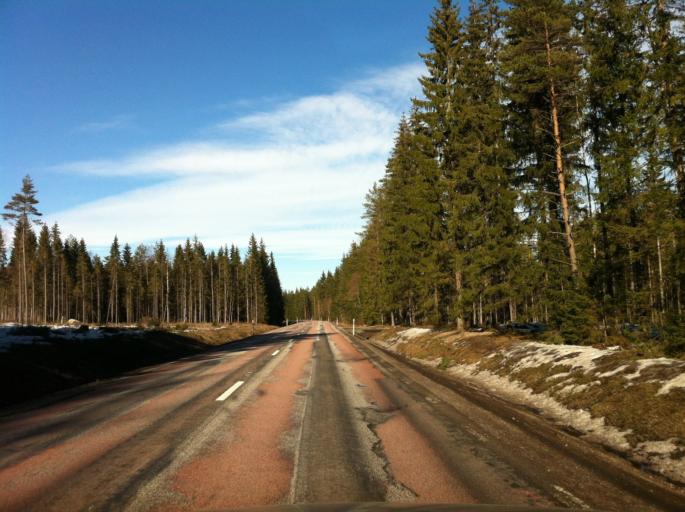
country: SE
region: Vaermland
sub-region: Filipstads Kommun
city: Filipstad
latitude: 59.7399
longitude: 14.2301
